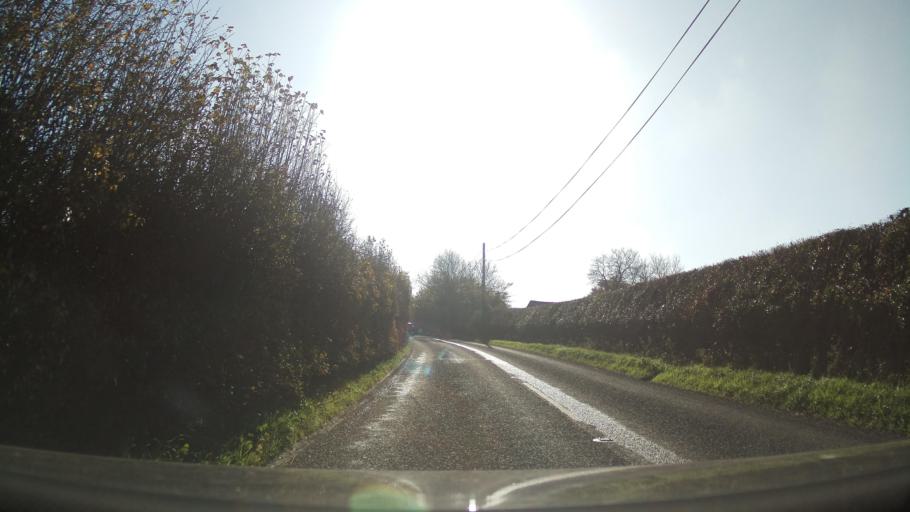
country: GB
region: England
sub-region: Somerset
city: Bruton
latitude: 51.1605
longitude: -2.4170
